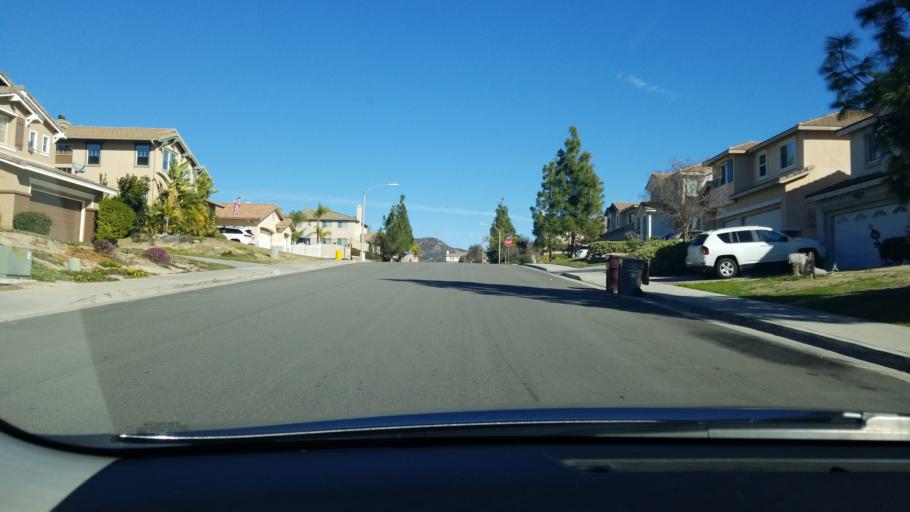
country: US
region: California
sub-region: Riverside County
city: Murrieta
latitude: 33.5874
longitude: -117.2228
